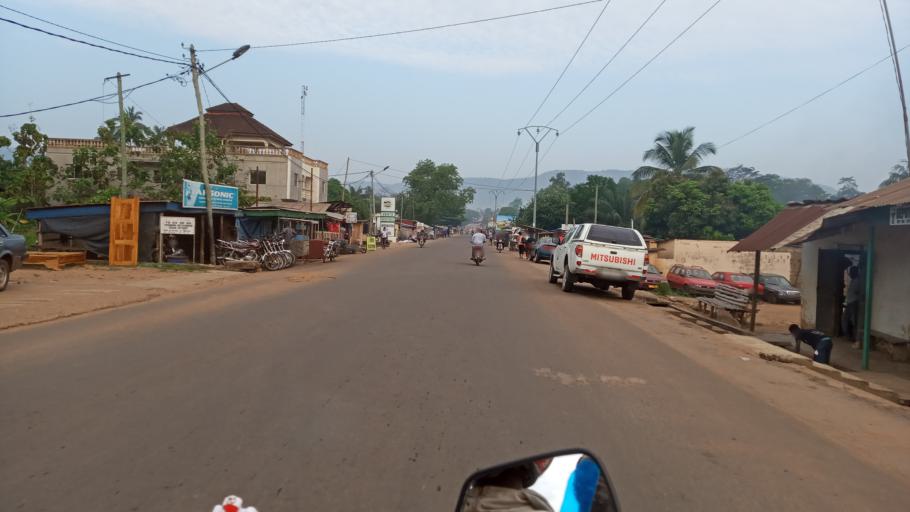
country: TG
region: Plateaux
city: Kpalime
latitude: 6.8999
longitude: 0.6351
